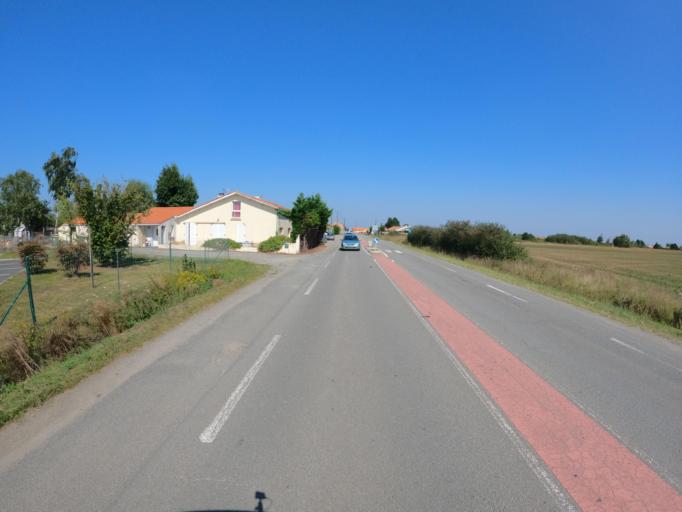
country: FR
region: Pays de la Loire
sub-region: Departement de la Loire-Atlantique
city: Les Sorinieres
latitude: 47.1141
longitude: -1.5407
